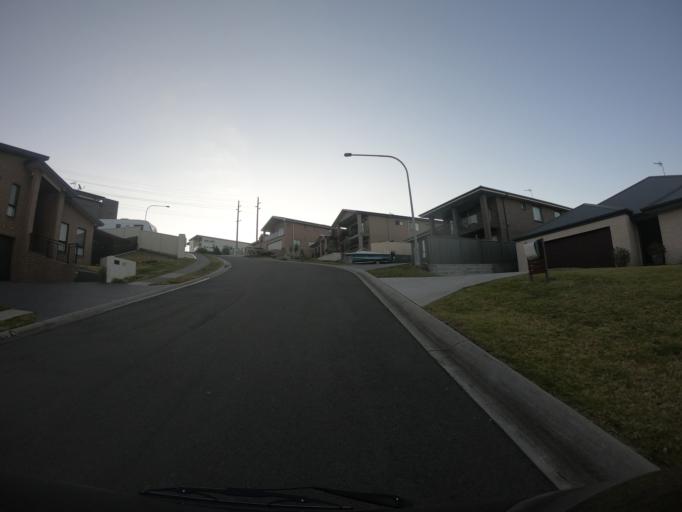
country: AU
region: New South Wales
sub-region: Wollongong
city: Lake Heights
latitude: -34.4770
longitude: 150.8656
